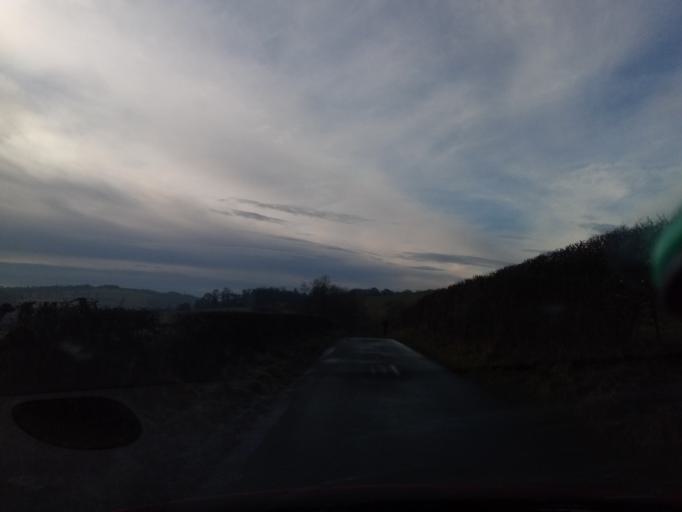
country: GB
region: Scotland
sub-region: The Scottish Borders
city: Hawick
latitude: 55.4474
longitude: -2.7431
